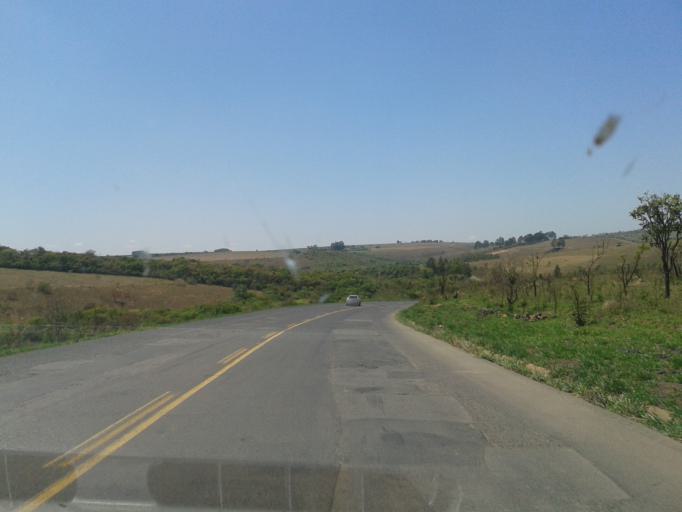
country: BR
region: Minas Gerais
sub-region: Araxa
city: Araxa
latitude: -19.4495
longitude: -47.1883
